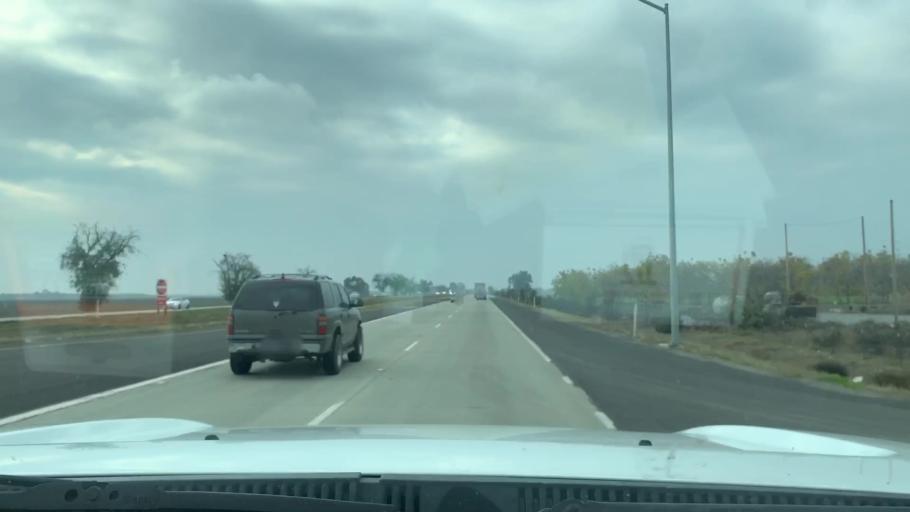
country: US
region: California
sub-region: Tulare County
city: Goshen
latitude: 36.3278
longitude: -119.4576
